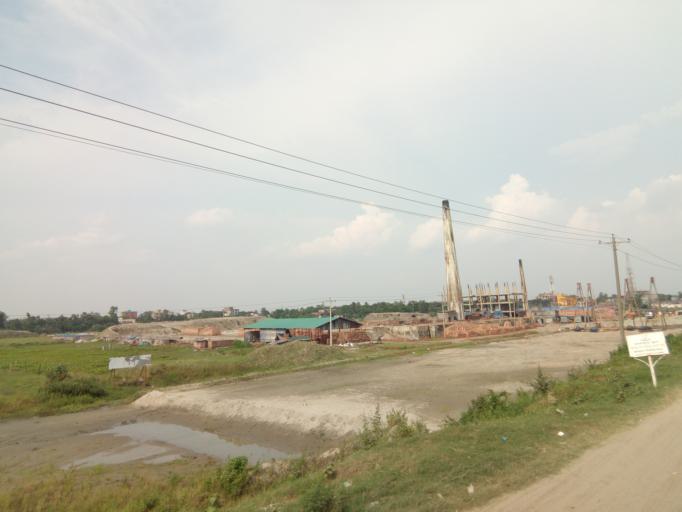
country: BD
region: Dhaka
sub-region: Dhaka
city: Dhaka
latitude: 23.6624
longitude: 90.3823
